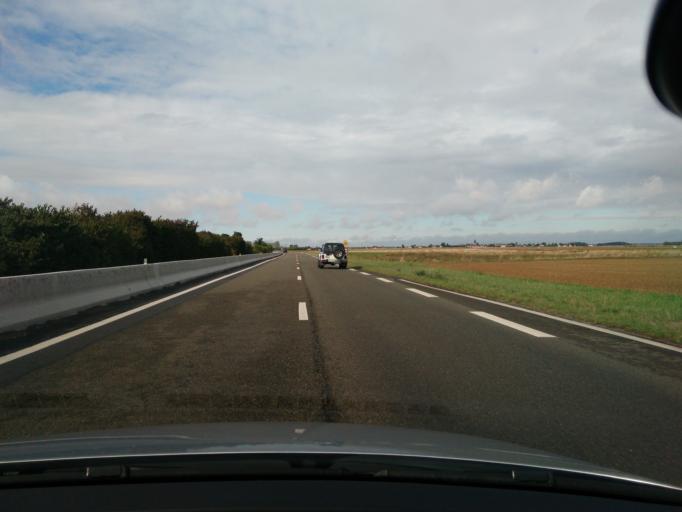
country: FR
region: Centre
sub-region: Departement d'Eure-et-Loir
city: Bu
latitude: 48.7608
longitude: 1.5093
